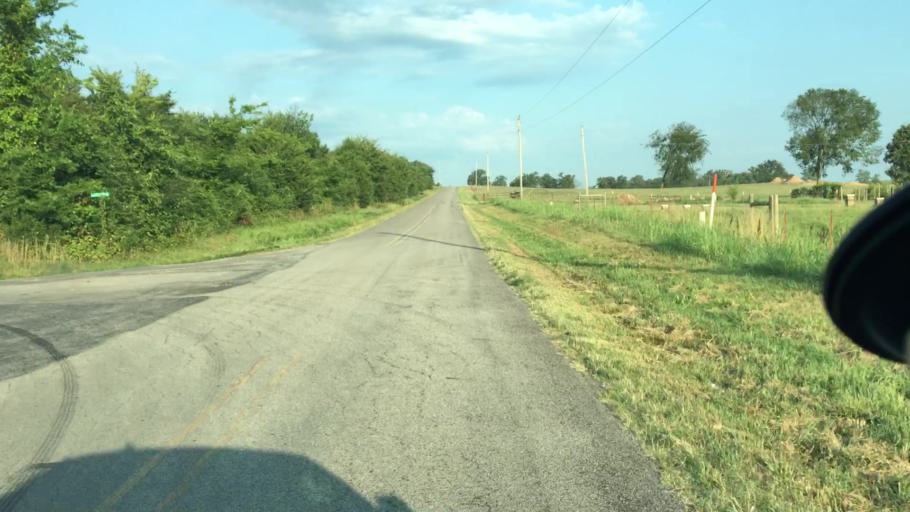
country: US
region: Arkansas
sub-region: Johnson County
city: Coal Hill
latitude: 35.3662
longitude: -93.6126
